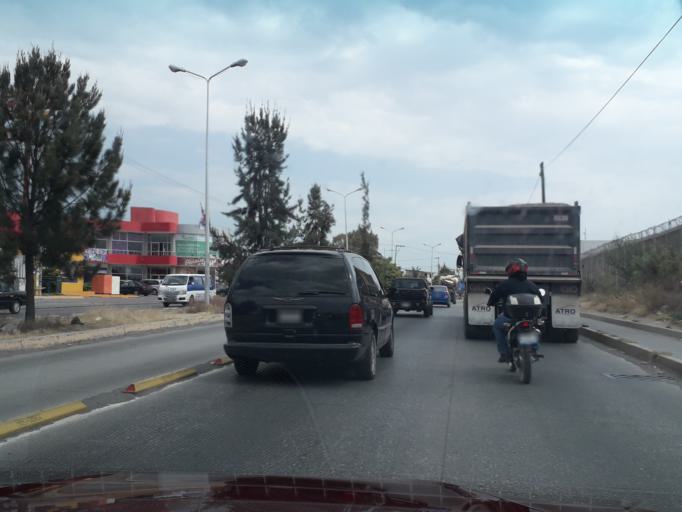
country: MX
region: Puebla
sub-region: Puebla
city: El Capulo (La Quebradora)
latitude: 18.9683
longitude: -98.2665
